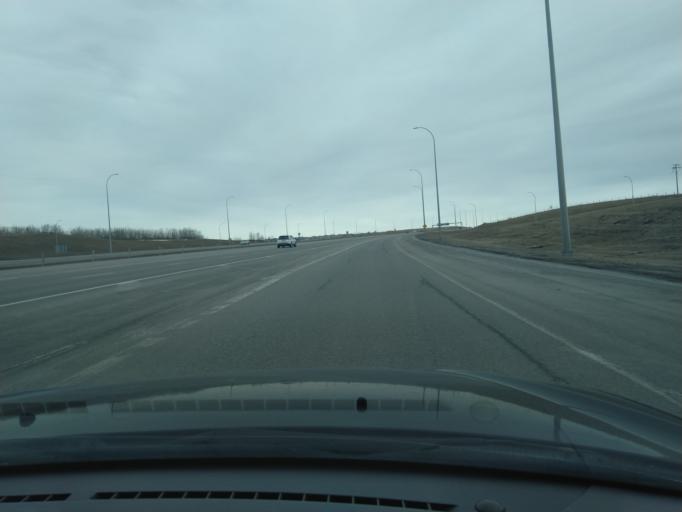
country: CA
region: Alberta
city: Calgary
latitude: 51.1325
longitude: -114.2254
